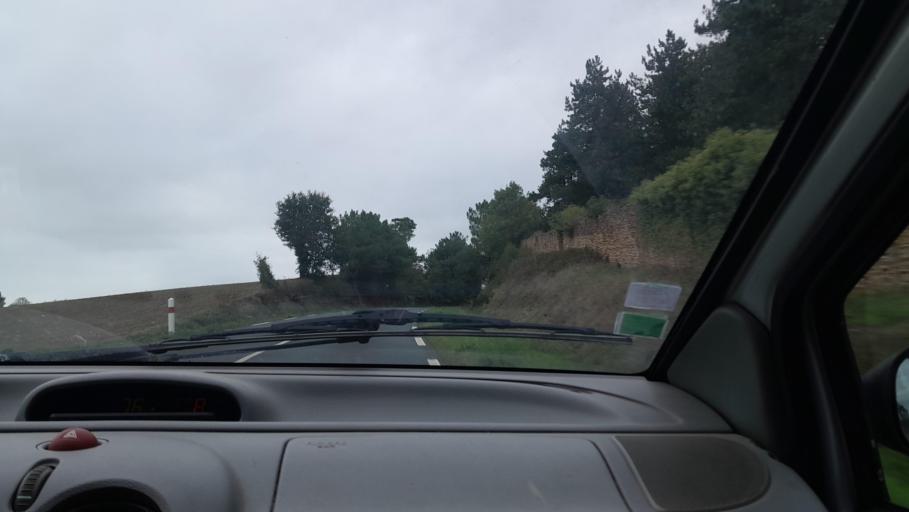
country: FR
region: Pays de la Loire
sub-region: Departement de la Loire-Atlantique
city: Saint-Mars-la-Jaille
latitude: 47.5042
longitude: -1.1803
